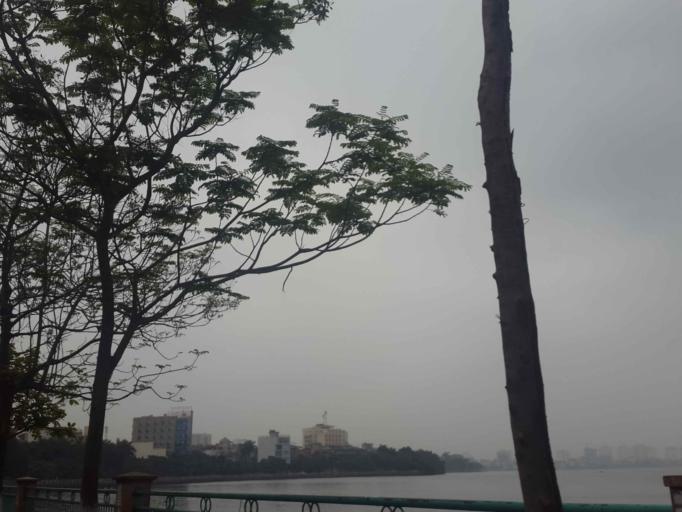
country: VN
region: Ha Noi
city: Cau Giay
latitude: 21.0450
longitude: 105.8170
